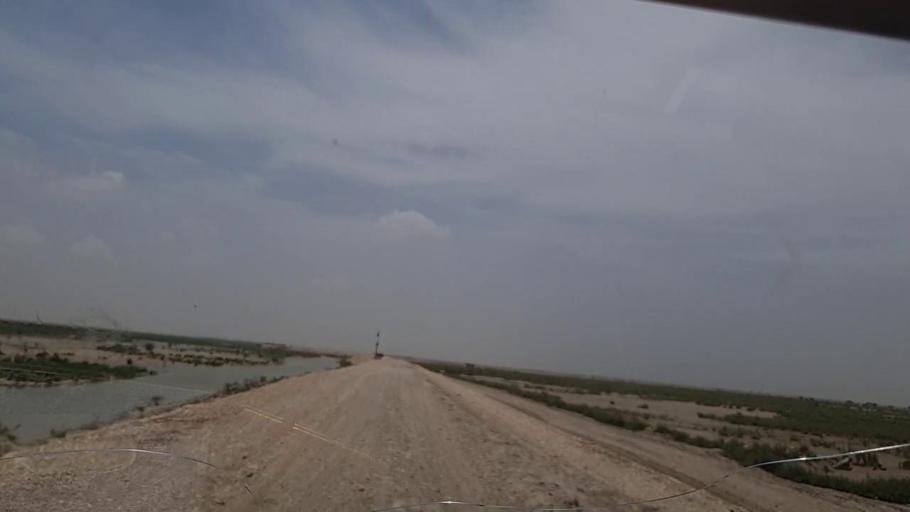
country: PK
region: Sindh
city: Bhan
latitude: 26.5053
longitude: 67.6332
